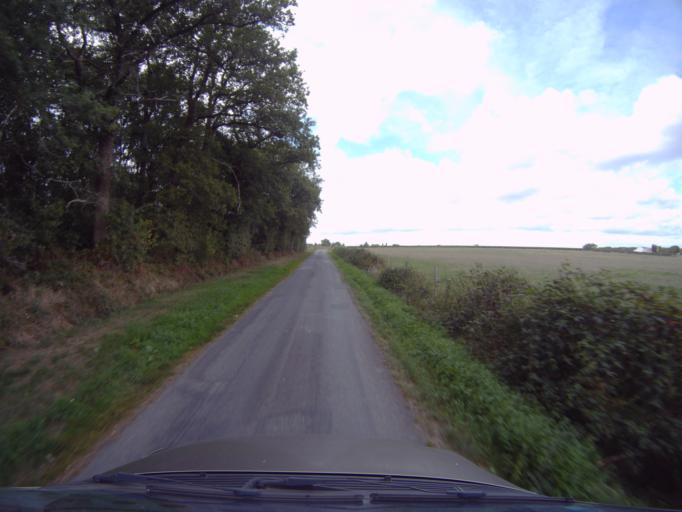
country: FR
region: Pays de la Loire
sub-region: Departement de la Loire-Atlantique
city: La Planche
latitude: 47.0319
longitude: -1.4162
